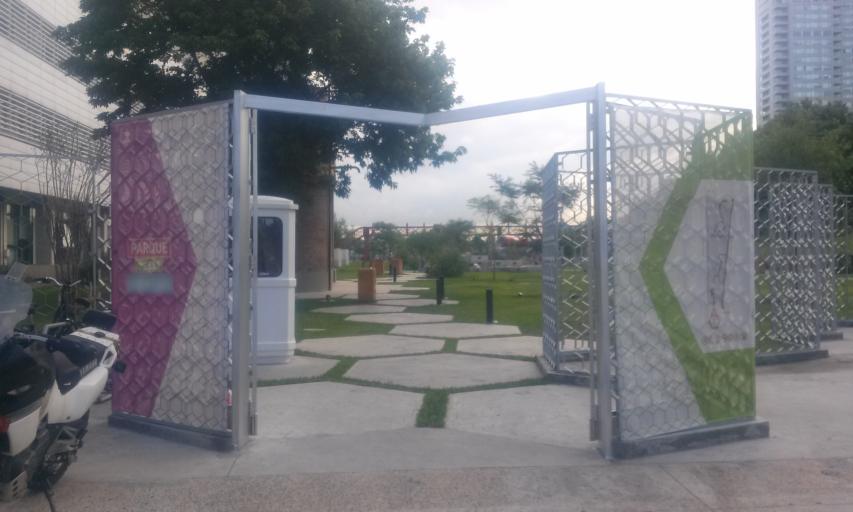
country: AR
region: Buenos Aires F.D.
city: Colegiales
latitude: -34.5814
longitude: -58.4286
